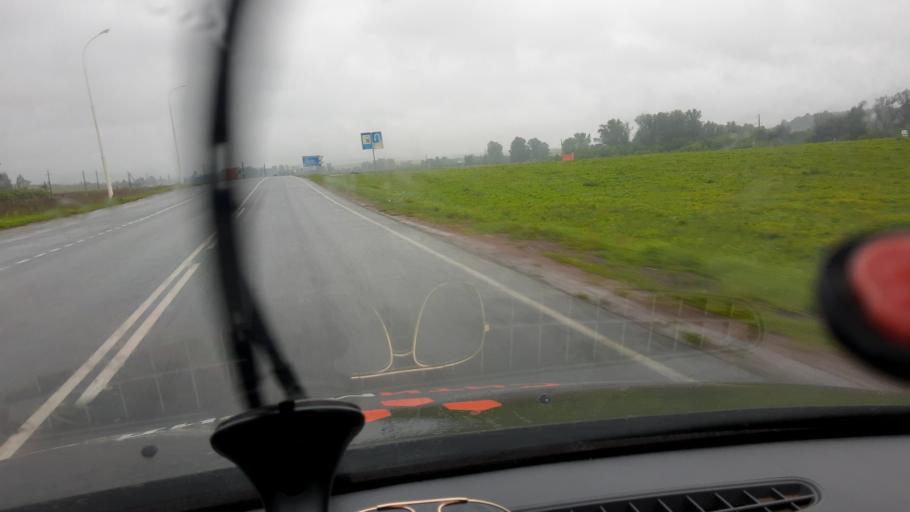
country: RU
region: Bashkortostan
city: Karmaskaly
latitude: 53.9329
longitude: 56.4196
